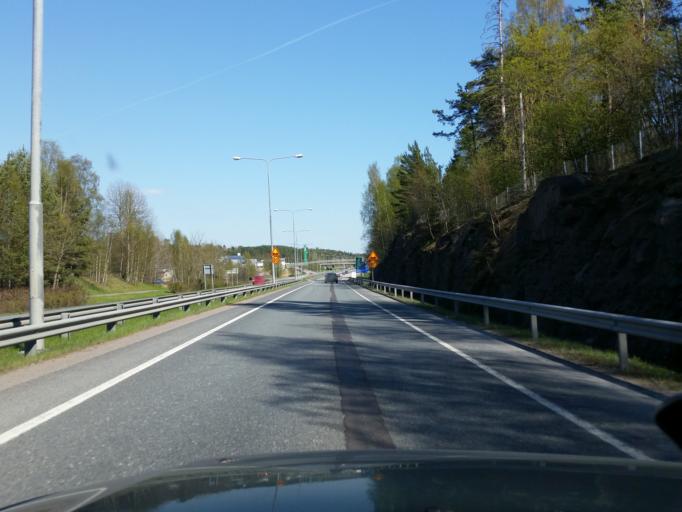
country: FI
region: Uusimaa
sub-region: Helsinki
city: Kirkkonummi
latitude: 60.1162
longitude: 24.4298
